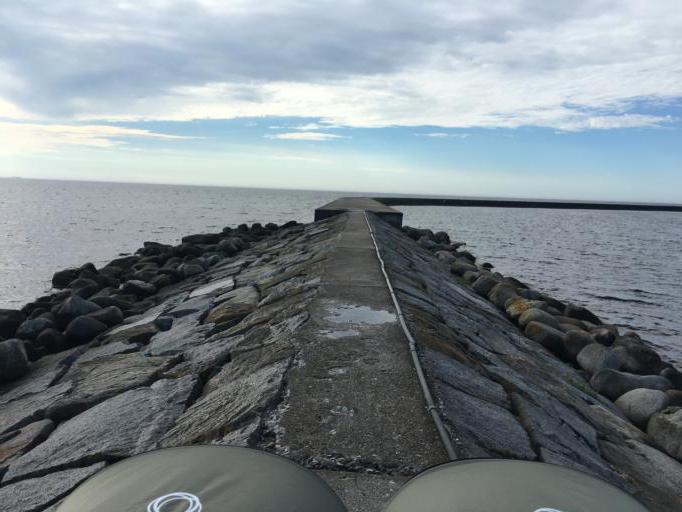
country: SE
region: Skane
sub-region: Vellinge Kommun
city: Hollviken
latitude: 55.3961
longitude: 12.9504
